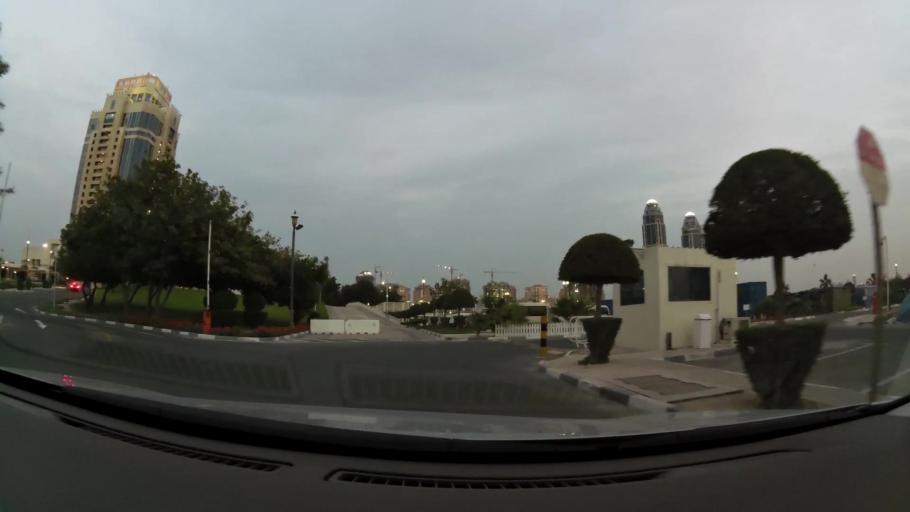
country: QA
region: Baladiyat ad Dawhah
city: Doha
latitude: 25.3791
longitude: 51.5295
